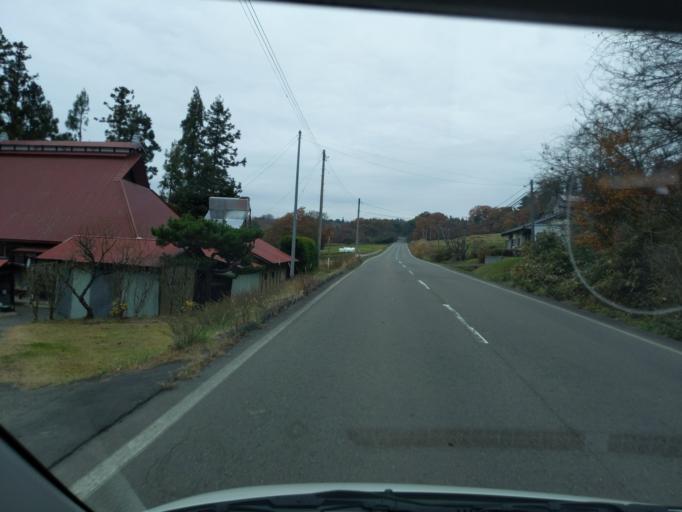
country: JP
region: Iwate
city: Kitakami
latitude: 39.2262
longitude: 141.2220
